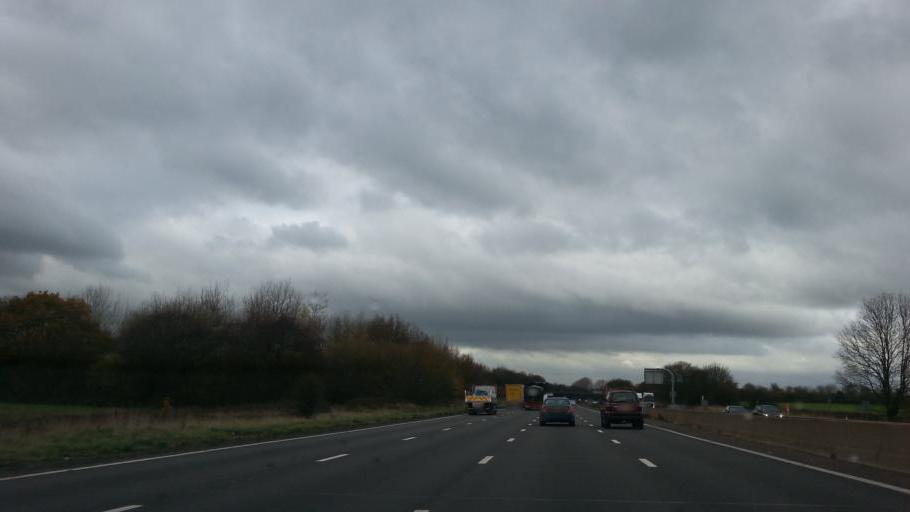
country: GB
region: England
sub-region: Staffordshire
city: Penkridge
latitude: 52.7120
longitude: -2.1012
